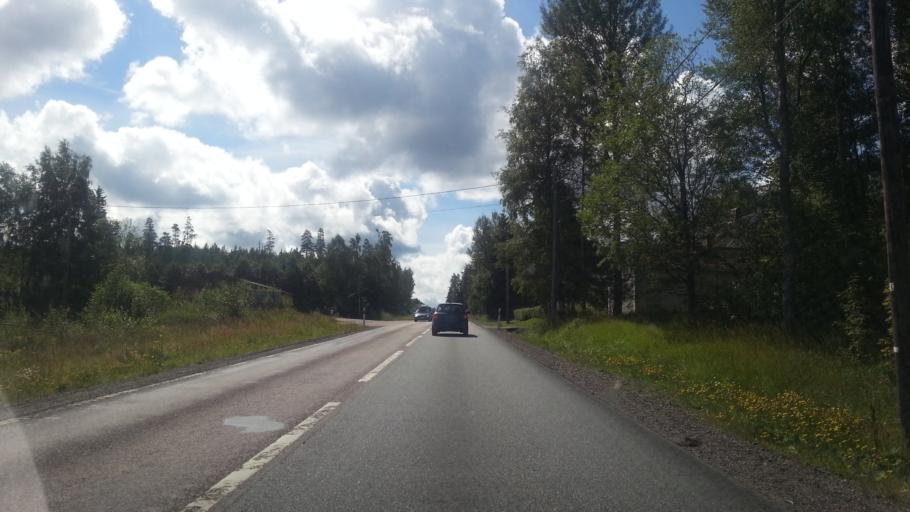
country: SE
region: Dalarna
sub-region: Ludvika Kommun
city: Grangesberg
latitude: 60.0641
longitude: 14.9860
